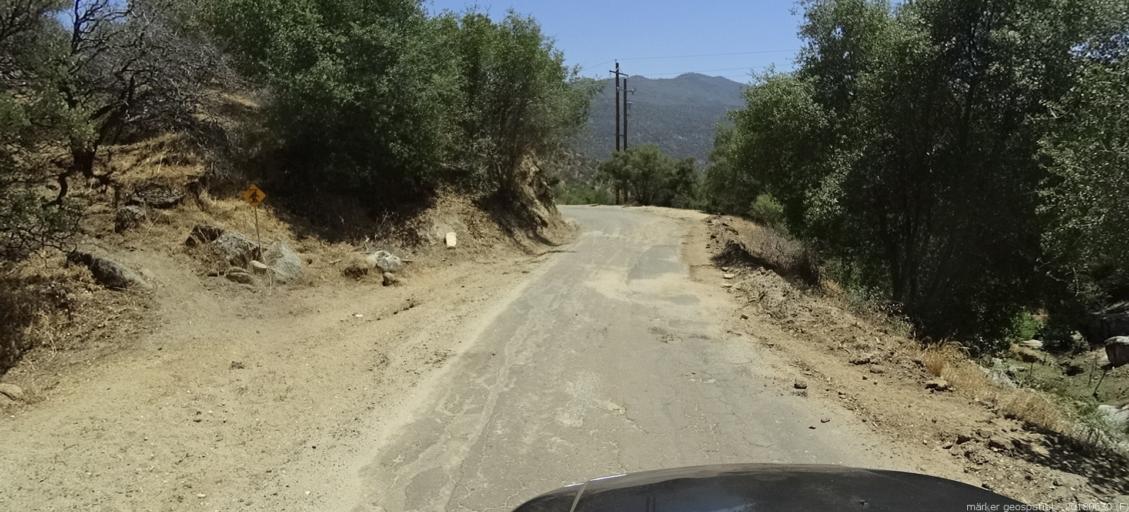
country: US
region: California
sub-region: Fresno County
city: Auberry
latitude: 37.1693
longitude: -119.4337
